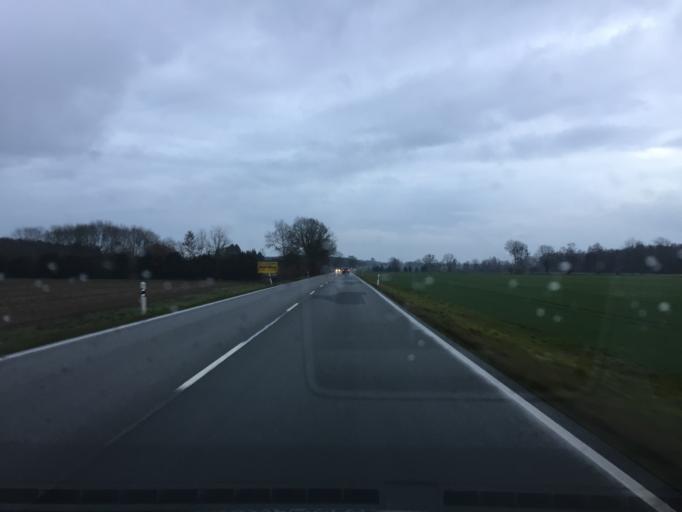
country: DE
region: Lower Saxony
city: Uchte
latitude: 52.5223
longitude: 8.8920
